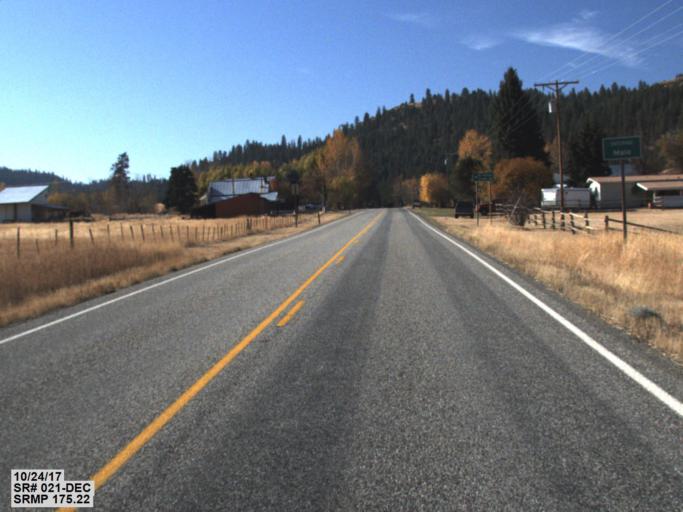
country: US
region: Washington
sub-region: Ferry County
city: Republic
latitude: 48.8027
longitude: -118.6065
